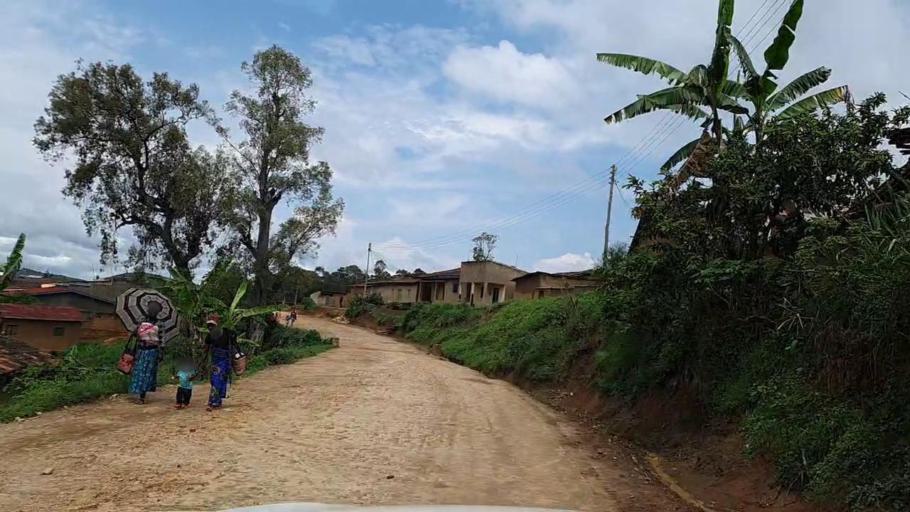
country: RW
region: Southern Province
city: Gikongoro
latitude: -2.3301
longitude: 29.5301
